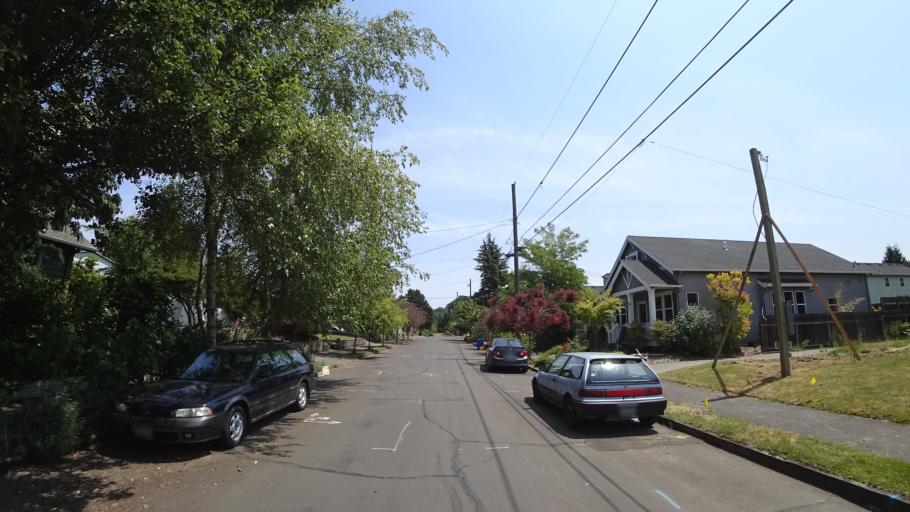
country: US
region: Oregon
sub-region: Multnomah County
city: Portland
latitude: 45.5807
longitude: -122.6754
